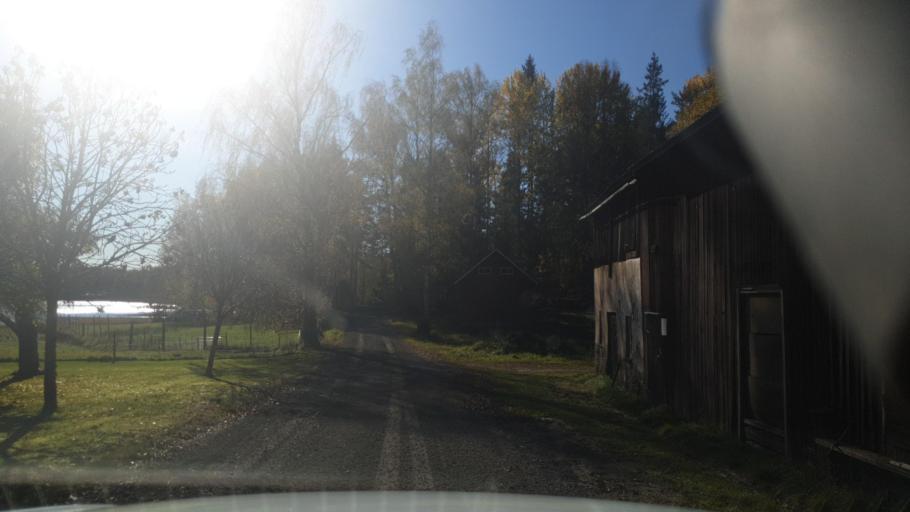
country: SE
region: Vaermland
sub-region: Grums Kommun
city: Grums
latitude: 59.5100
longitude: 12.9283
